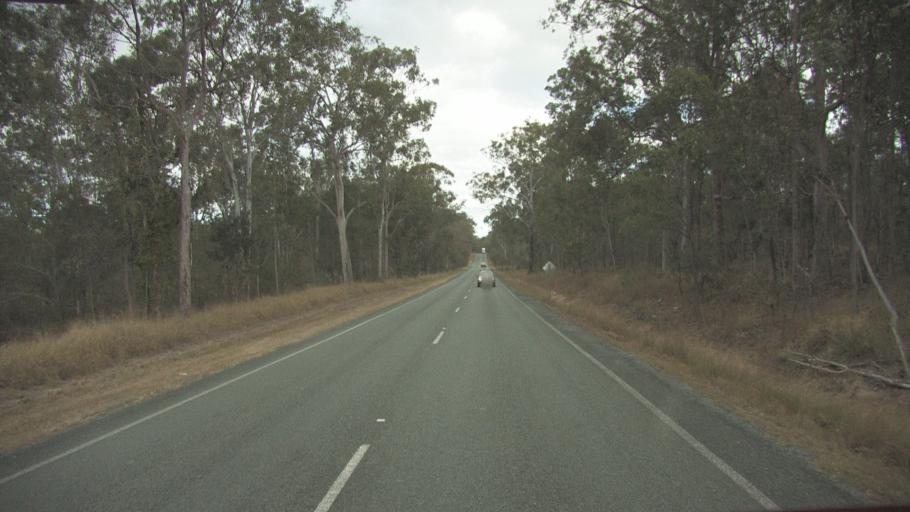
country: AU
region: Queensland
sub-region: Logan
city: Cedar Vale
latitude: -27.9031
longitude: 153.0907
